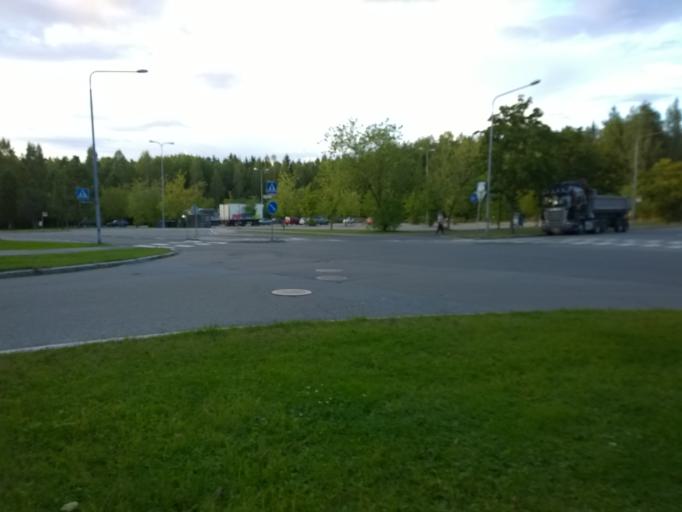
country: FI
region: Pirkanmaa
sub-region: Tampere
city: Tampere
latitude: 61.4472
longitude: 23.8353
